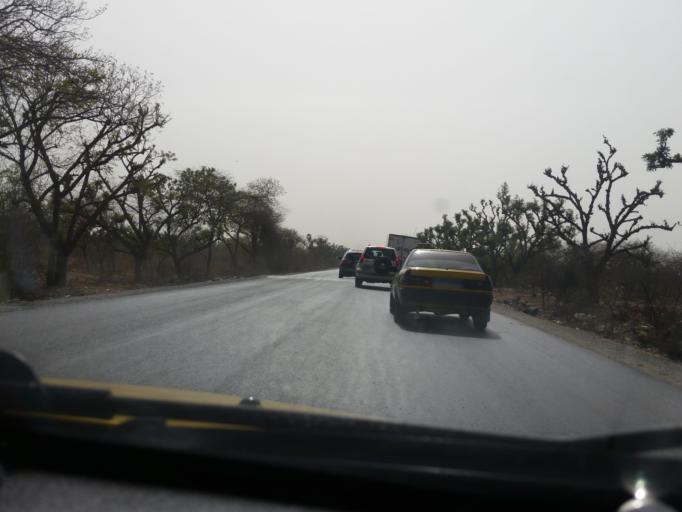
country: SN
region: Thies
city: Pout
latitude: 14.7626
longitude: -17.0276
